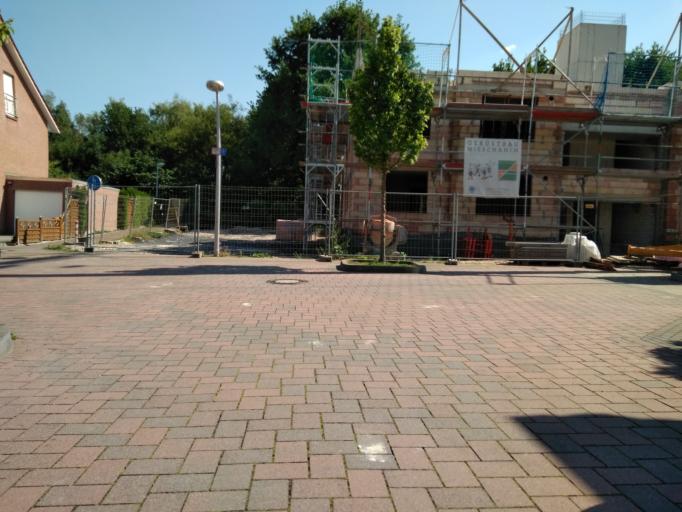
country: DE
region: North Rhine-Westphalia
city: Dorsten
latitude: 51.6750
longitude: 6.9384
